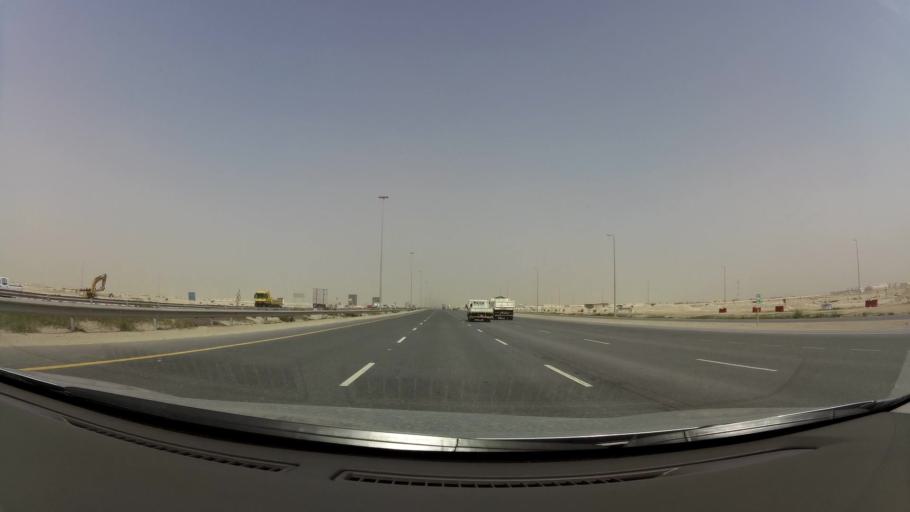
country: QA
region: Baladiyat ar Rayyan
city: Ar Rayyan
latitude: 25.1760
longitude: 51.3373
